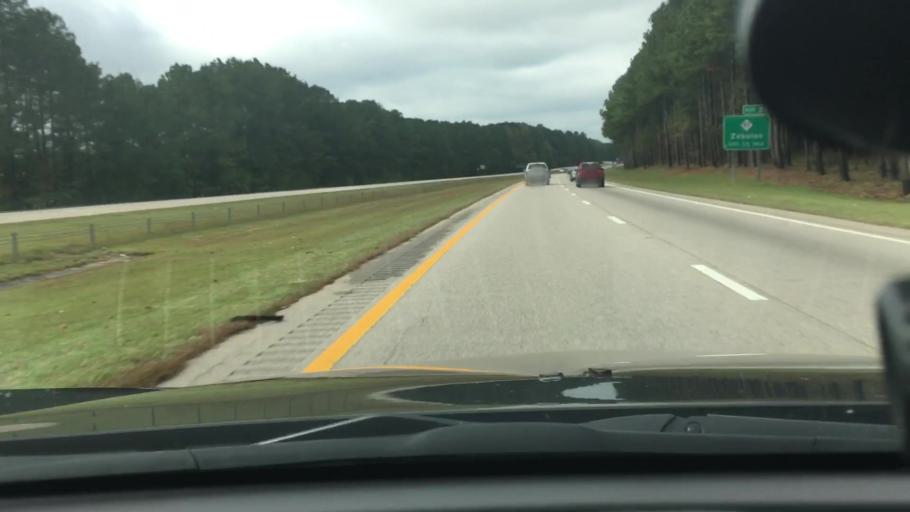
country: US
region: North Carolina
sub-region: Wake County
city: Zebulon
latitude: 35.8237
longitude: -78.2796
